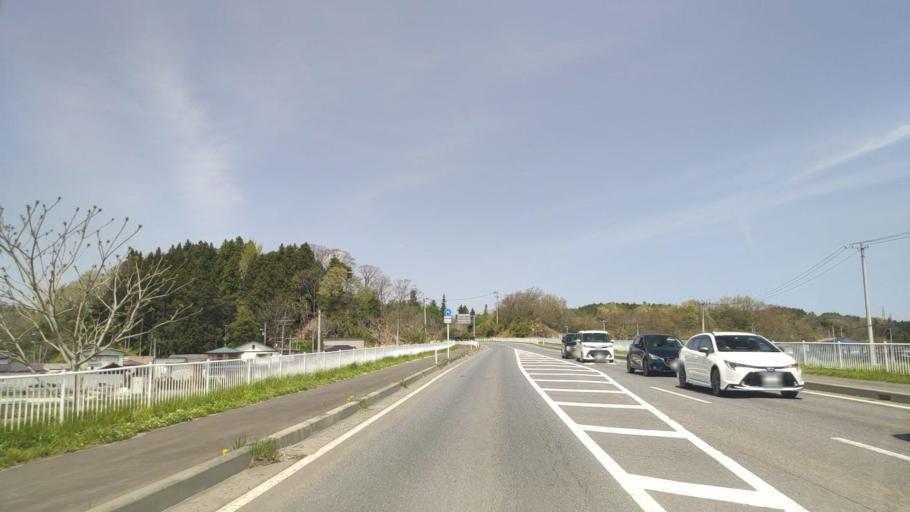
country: JP
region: Aomori
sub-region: Hachinohe Shi
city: Uchimaru
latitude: 40.5180
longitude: 141.4266
